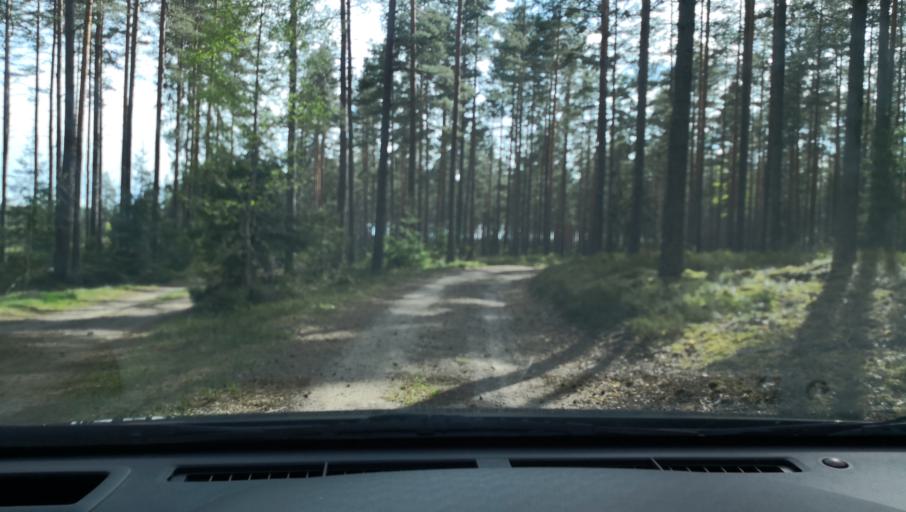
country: SE
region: OErebro
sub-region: Askersunds Kommun
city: Asbro
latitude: 59.0257
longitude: 15.0543
